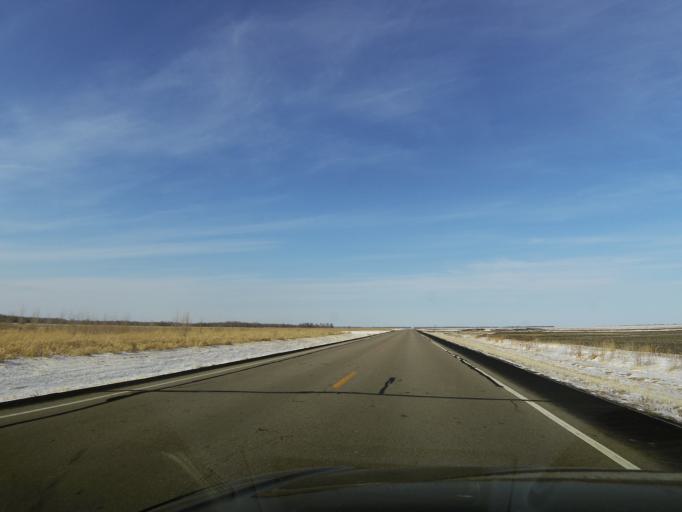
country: US
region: North Dakota
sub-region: Walsh County
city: Grafton
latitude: 48.4259
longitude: -97.1072
